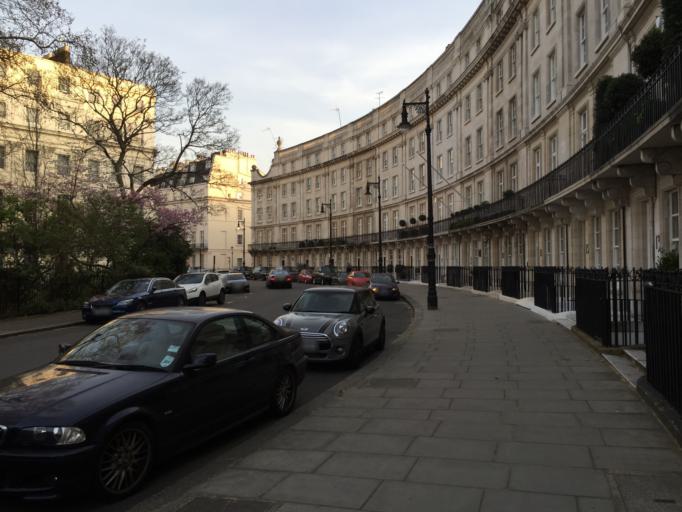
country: GB
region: England
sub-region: Greater London
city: Chelsea
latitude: 51.5007
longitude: -0.1561
